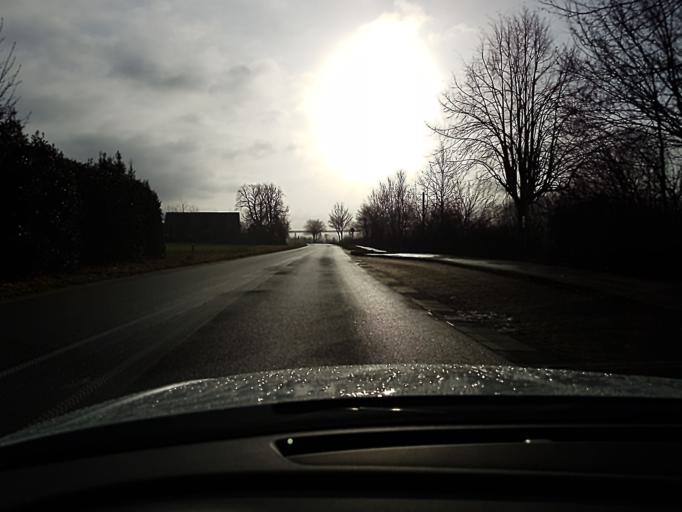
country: DE
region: North Rhine-Westphalia
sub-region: Regierungsbezirk Dusseldorf
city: Muelheim (Ruhr)
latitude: 51.3975
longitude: 6.9014
